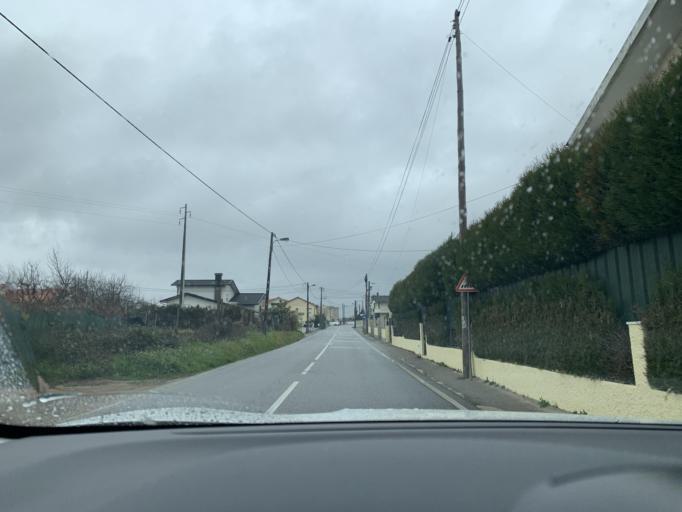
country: PT
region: Viseu
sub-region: Viseu
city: Rio de Loba
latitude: 40.6342
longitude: -7.8660
